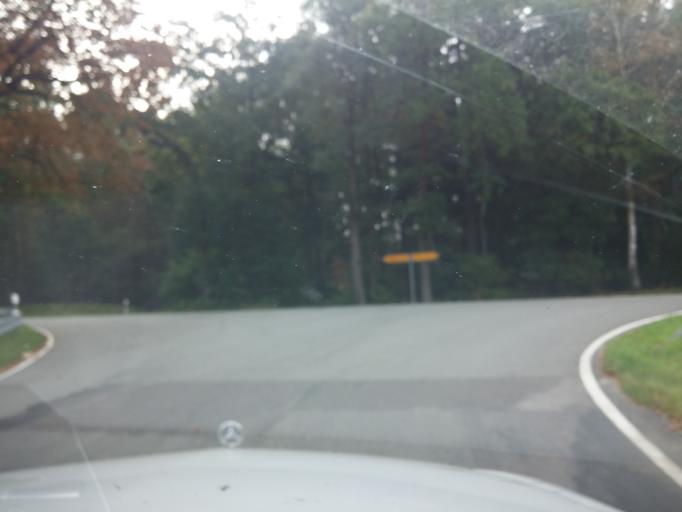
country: DE
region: Brandenburg
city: Putlitz
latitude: 53.2779
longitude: 12.0669
